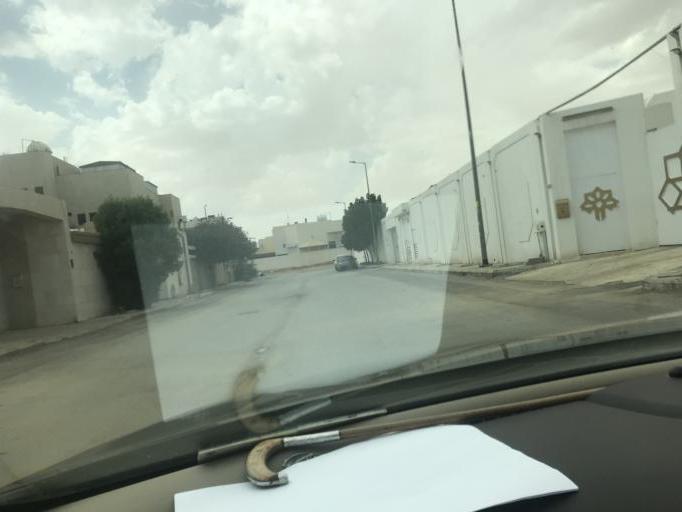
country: SA
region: Ar Riyad
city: Riyadh
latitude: 24.7283
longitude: 46.7810
